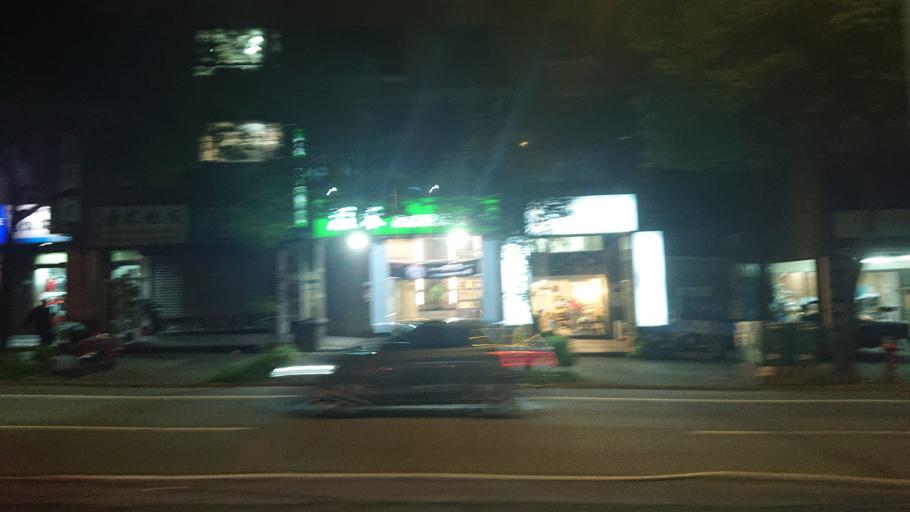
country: TW
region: Taiwan
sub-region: Taoyuan
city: Taoyuan
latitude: 24.9338
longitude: 121.3754
